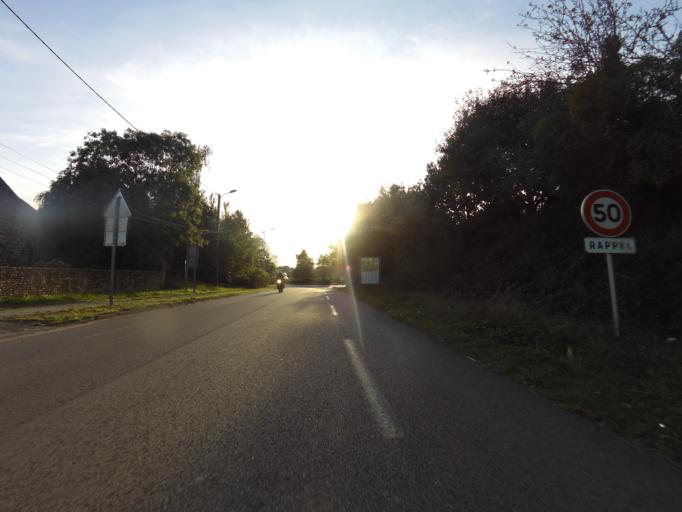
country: FR
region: Brittany
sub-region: Departement du Morbihan
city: Theix
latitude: 47.6286
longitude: -2.6421
